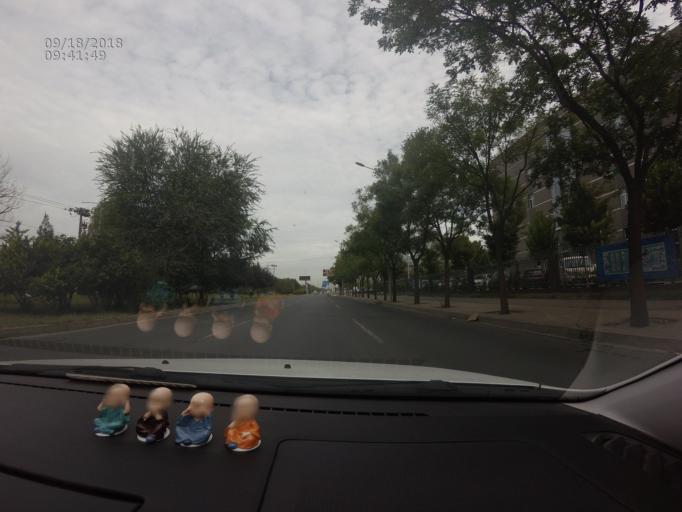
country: CN
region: Beijing
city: Xibeiwang
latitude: 40.0691
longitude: 116.2400
